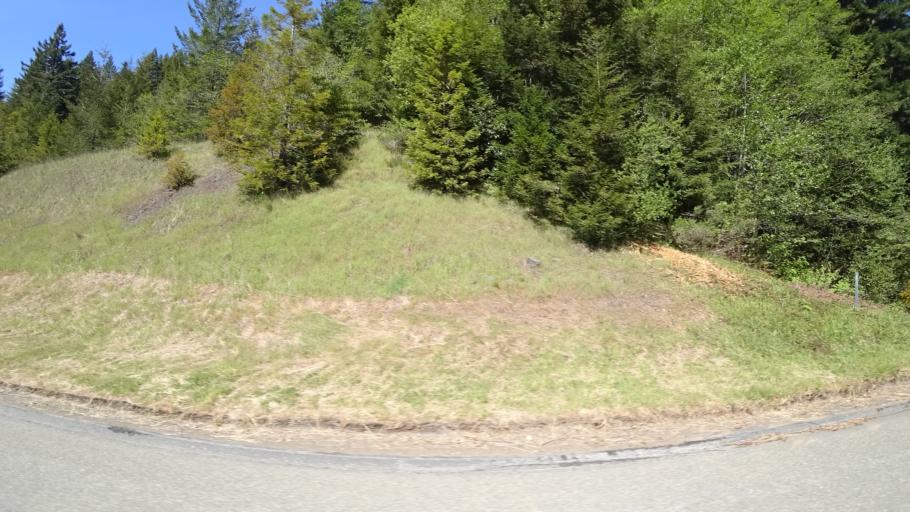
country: US
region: California
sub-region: Del Norte County
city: Bertsch-Oceanview
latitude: 41.4176
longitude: -123.9978
